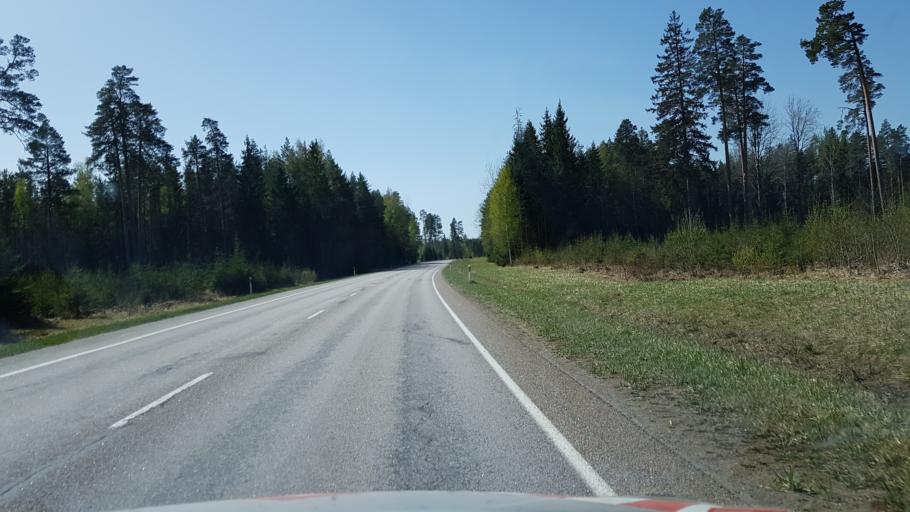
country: EE
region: Valgamaa
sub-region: Valga linn
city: Valga
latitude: 57.8306
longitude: 26.0577
